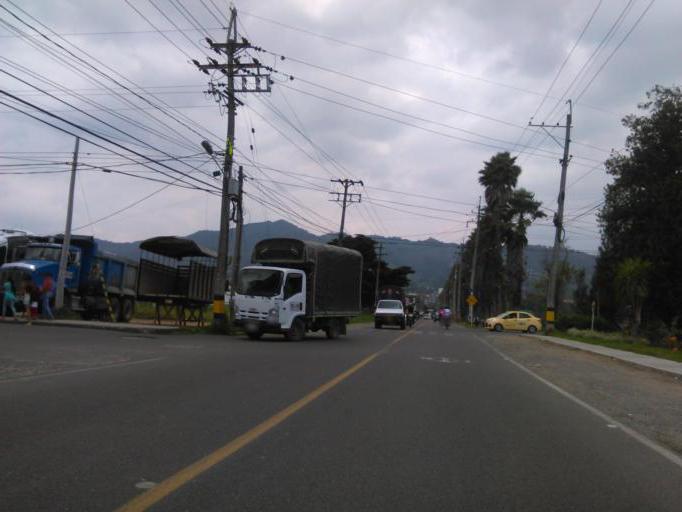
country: CO
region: Antioquia
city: La Ceja
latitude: 6.0280
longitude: -75.4241
